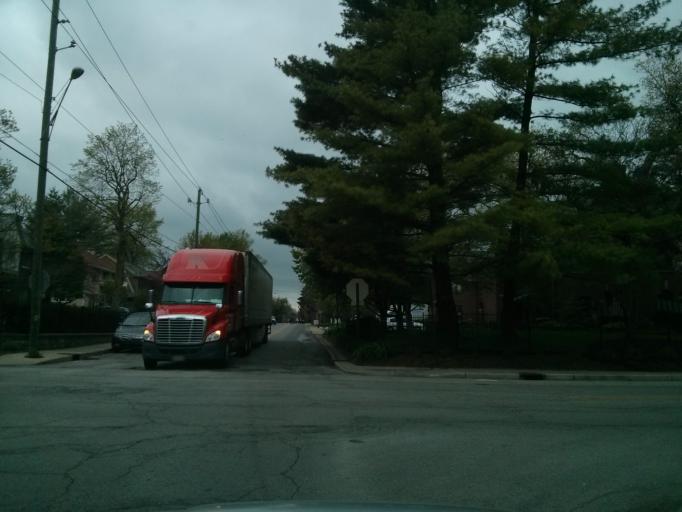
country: US
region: Indiana
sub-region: Marion County
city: Broad Ripple
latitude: 39.8469
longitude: -86.1545
